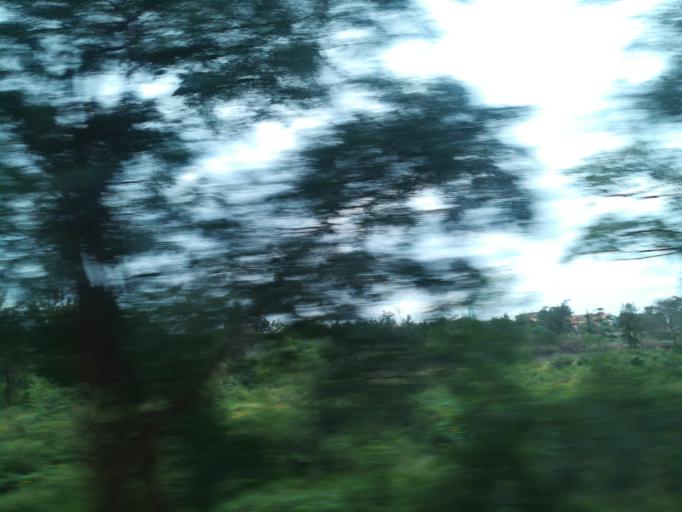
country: KE
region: Nairobi Area
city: Thika
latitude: -1.0392
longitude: 37.0599
